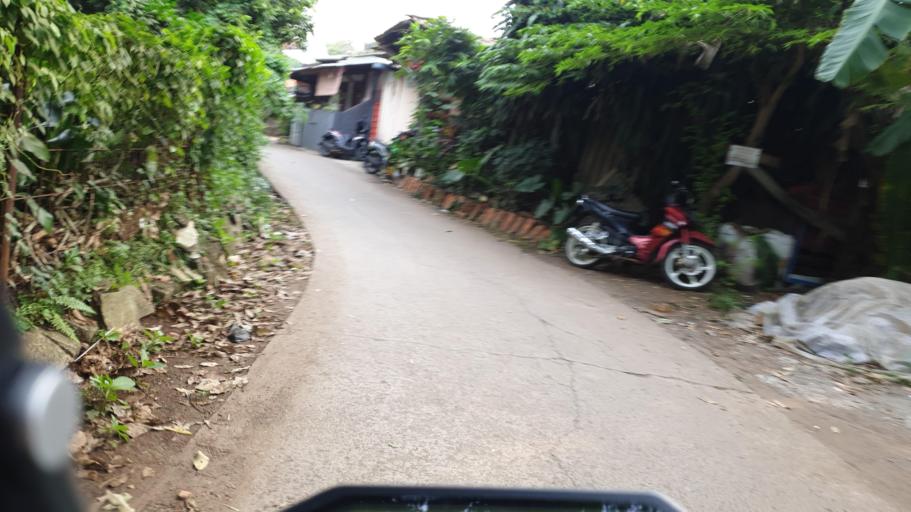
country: ID
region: West Java
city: Depok
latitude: -6.3372
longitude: 106.8317
